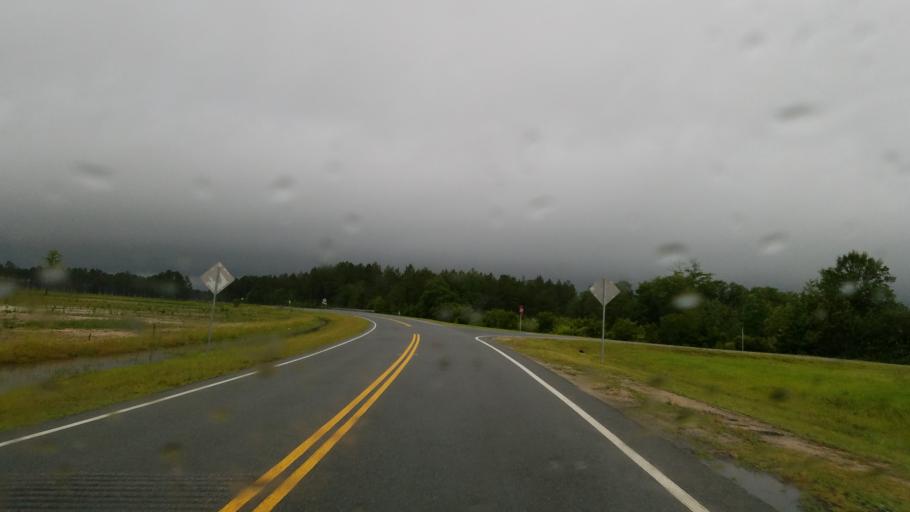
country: US
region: Georgia
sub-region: Lanier County
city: Lakeland
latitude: 31.0463
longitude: -83.0260
